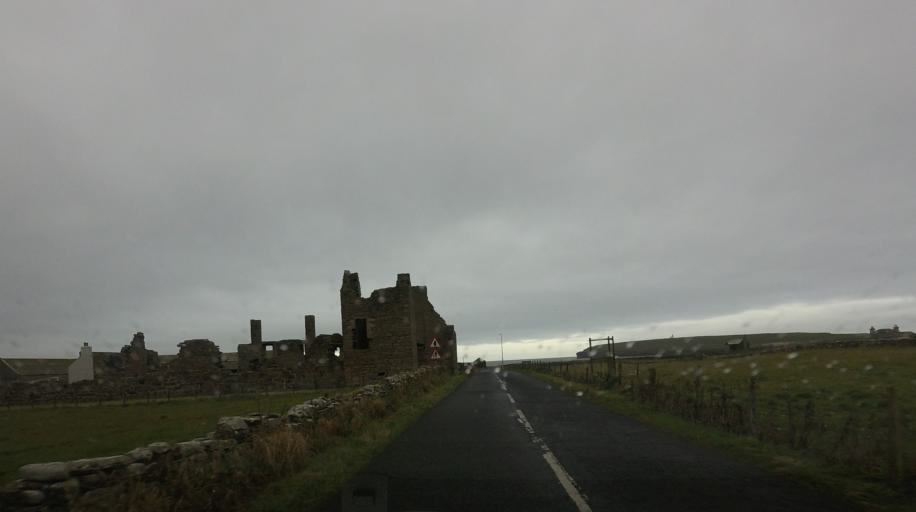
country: GB
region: Scotland
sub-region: Orkney Islands
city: Stromness
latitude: 59.1302
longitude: -3.3142
